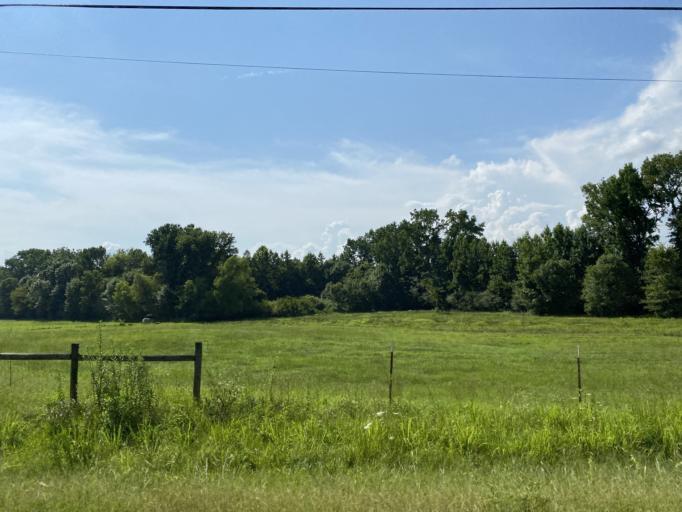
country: US
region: Alabama
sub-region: Lawrence County
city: Town Creek
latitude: 34.6276
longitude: -87.4116
